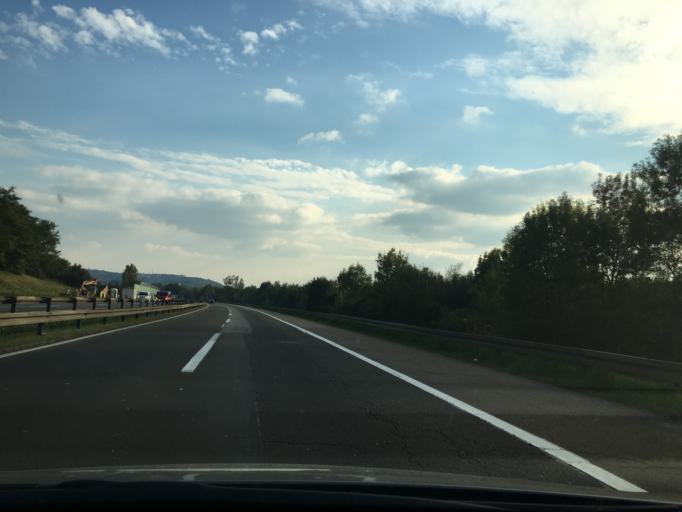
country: RS
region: Central Serbia
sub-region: Belgrade
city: Zvezdara
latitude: 44.6871
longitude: 20.5843
